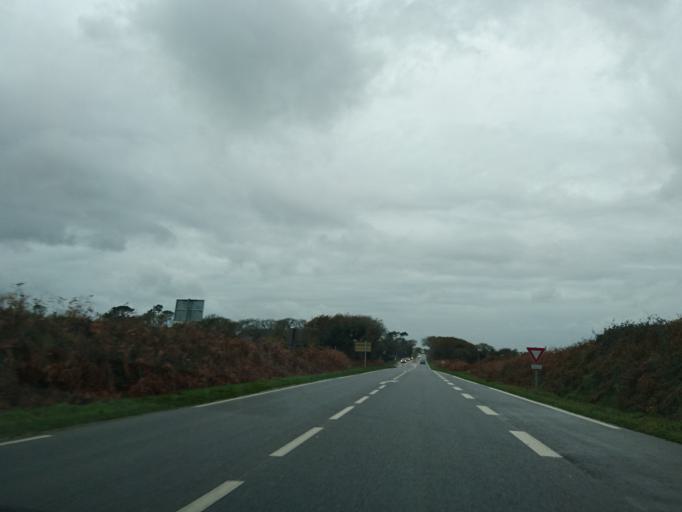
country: FR
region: Brittany
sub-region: Departement du Finistere
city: Plouzane
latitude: 48.3606
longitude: -4.6477
